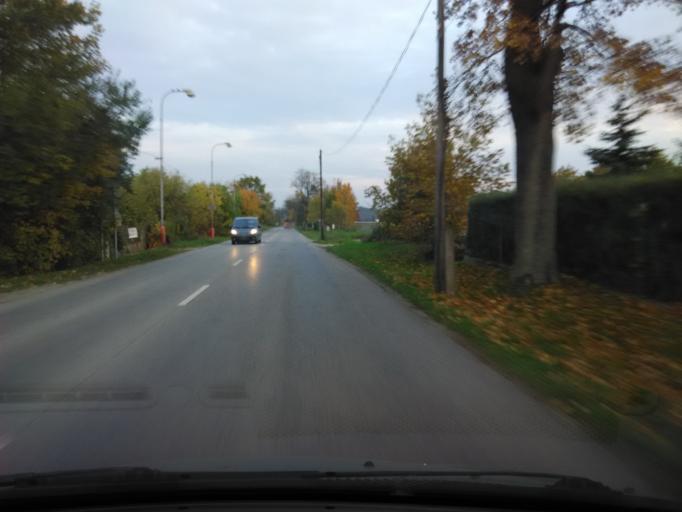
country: SK
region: Nitriansky
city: Levice
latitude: 48.2199
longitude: 18.6247
